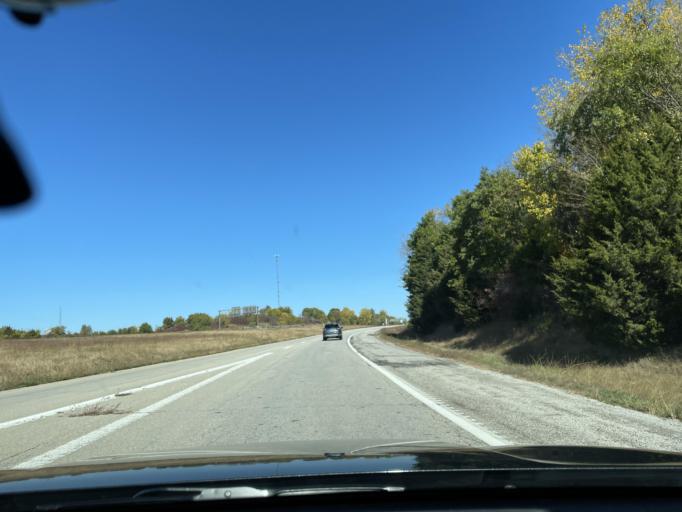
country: US
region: Missouri
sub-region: Andrew County
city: Savannah
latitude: 39.8875
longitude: -94.8564
